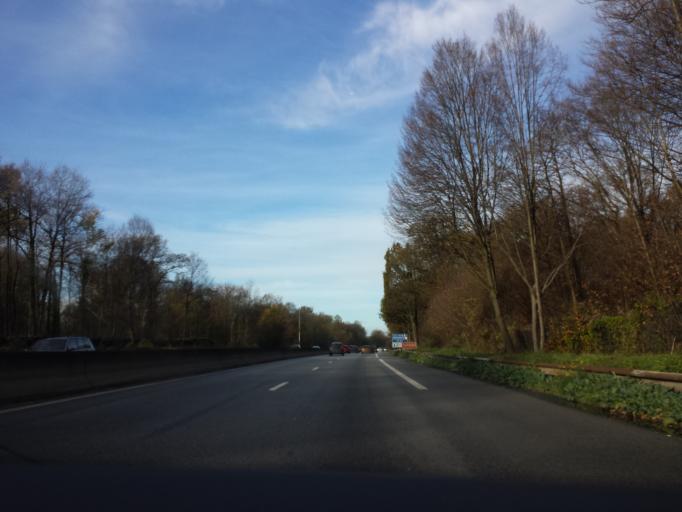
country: FR
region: Ile-de-France
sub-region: Departement des Yvelines
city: Noisy-le-Roi
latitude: 48.8495
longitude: 2.0708
